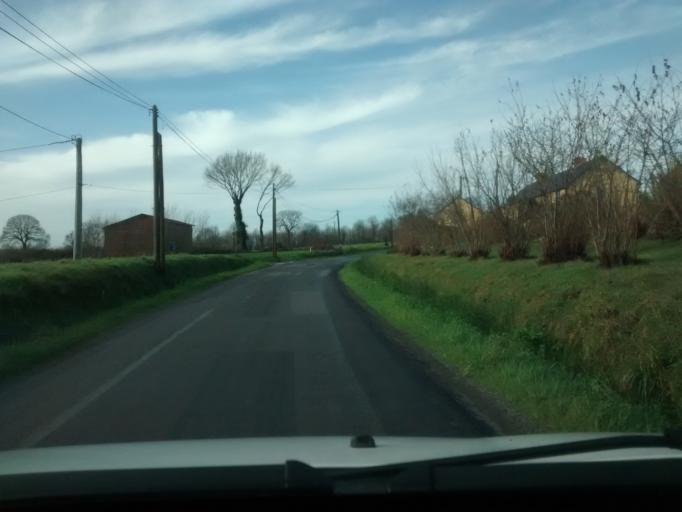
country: FR
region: Brittany
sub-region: Departement d'Ille-et-Vilaine
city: Montgermont
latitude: 48.1404
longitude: -1.7301
